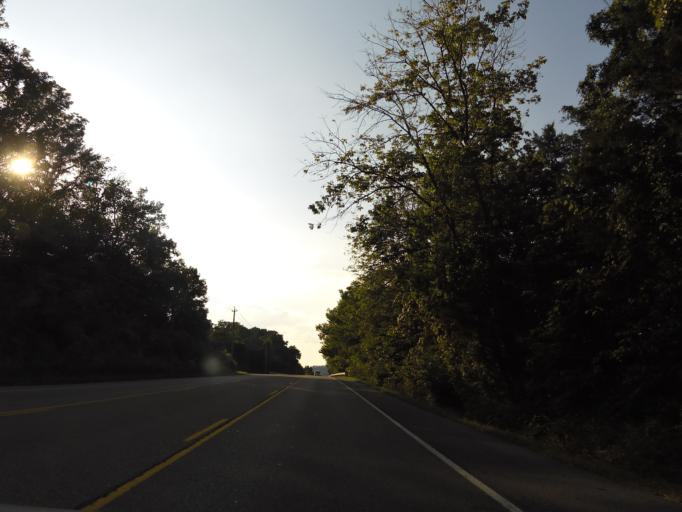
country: US
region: Tennessee
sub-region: Sevier County
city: Seymour
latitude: 35.9542
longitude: -83.8122
